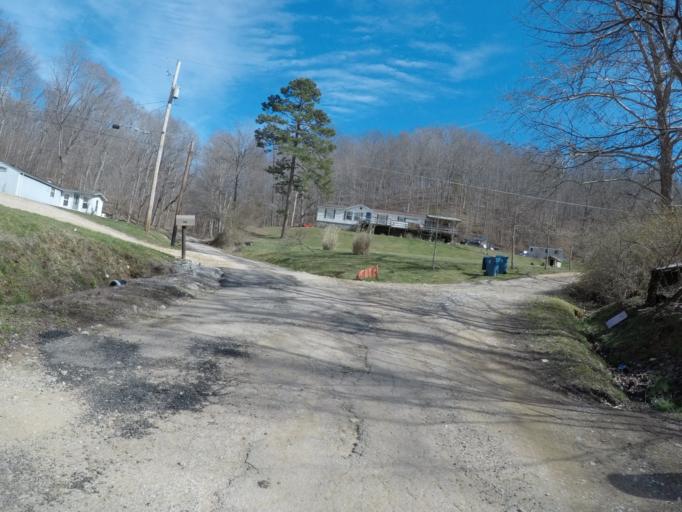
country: US
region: West Virginia
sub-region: Wayne County
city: Ceredo
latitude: 38.3477
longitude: -82.5536
